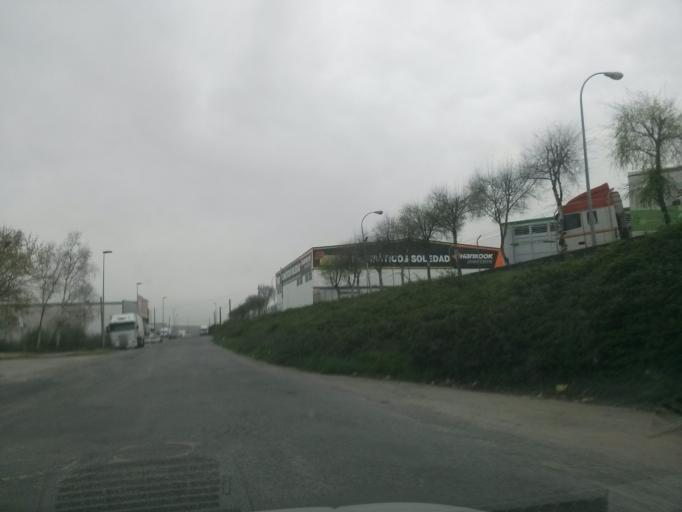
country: ES
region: Galicia
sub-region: Provincia de Lugo
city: Lugo
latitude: 43.0462
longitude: -7.5593
